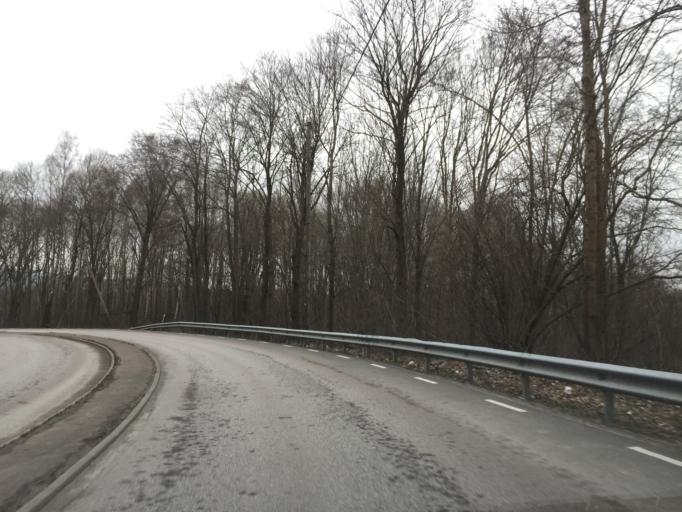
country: SE
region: Vaestra Goetaland
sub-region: Goteborg
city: Hammarkullen
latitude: 57.7605
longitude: 12.0138
